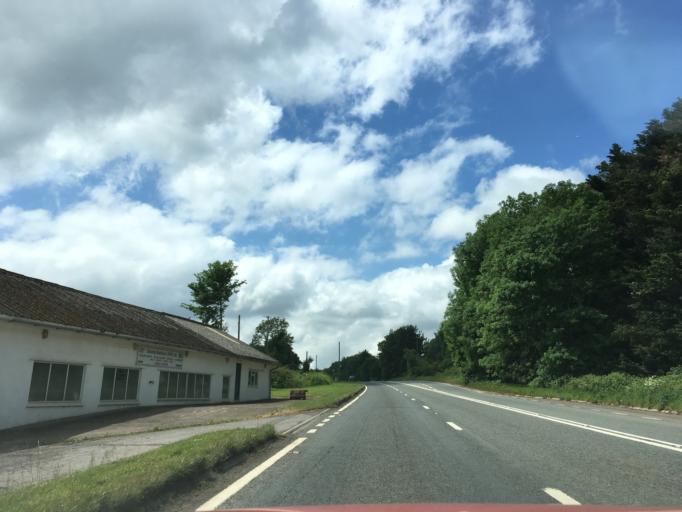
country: GB
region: England
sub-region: Devon
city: Uffculme
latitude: 50.9620
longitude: -3.2878
